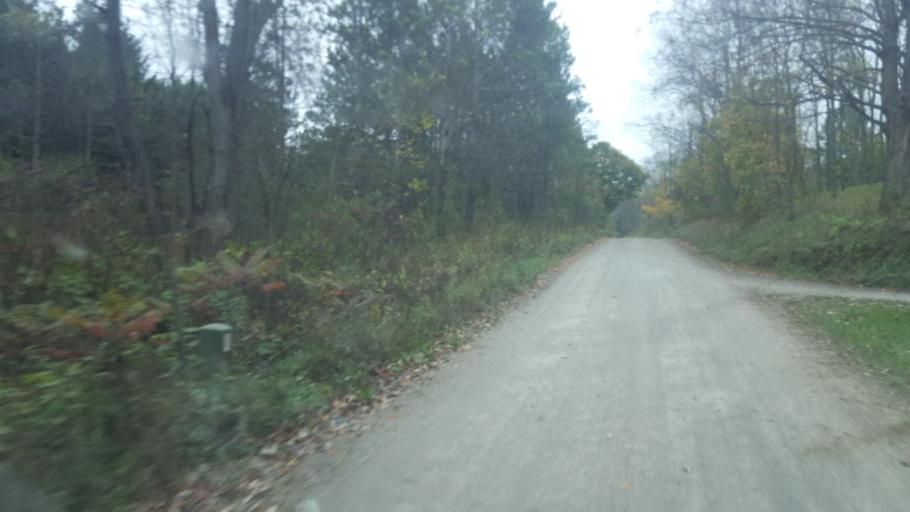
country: US
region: Ohio
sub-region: Harrison County
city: Cadiz
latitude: 40.3831
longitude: -81.0435
